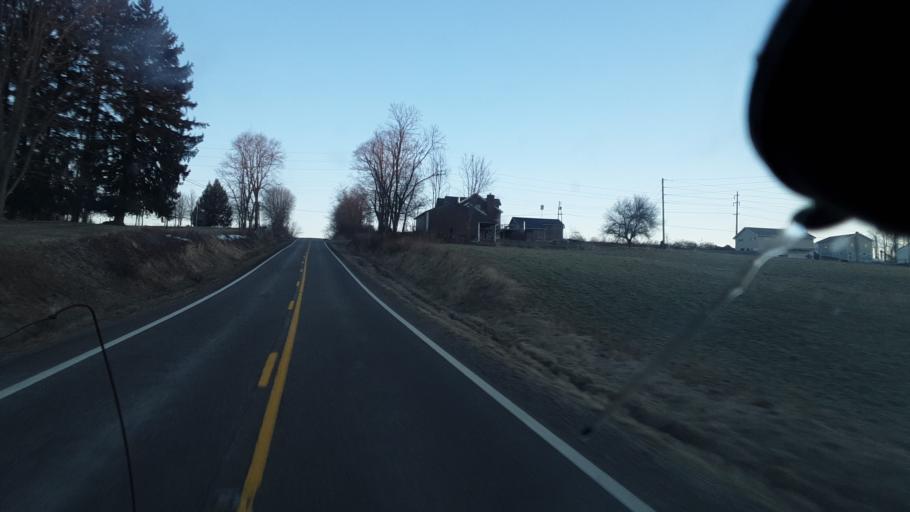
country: US
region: Ohio
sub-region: Perry County
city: Somerset
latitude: 39.7818
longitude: -82.3020
